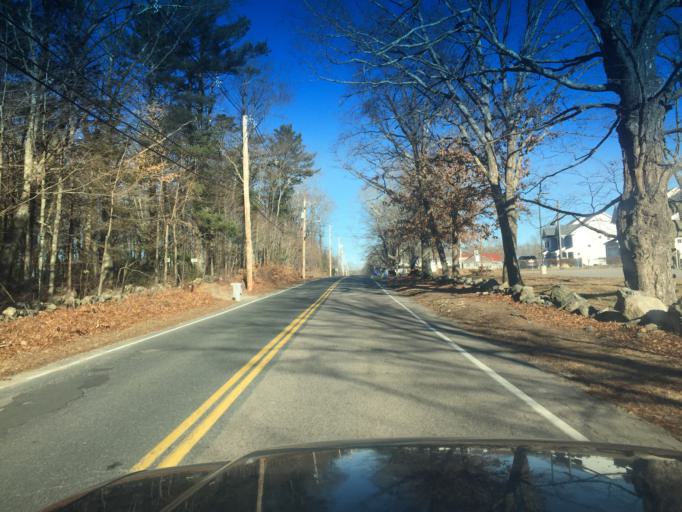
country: US
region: Massachusetts
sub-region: Middlesex County
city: Holliston
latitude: 42.1950
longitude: -71.4181
